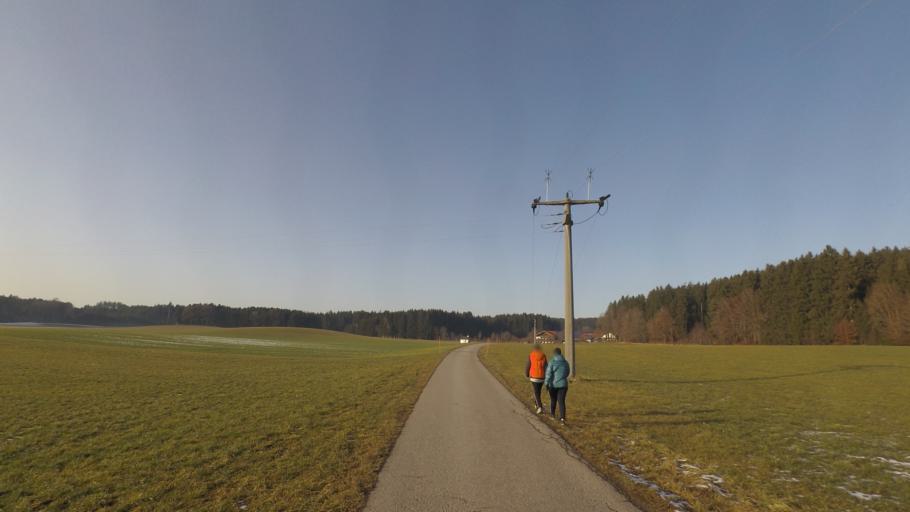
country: DE
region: Bavaria
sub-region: Upper Bavaria
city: Nussdorf
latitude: 47.9121
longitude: 12.5897
